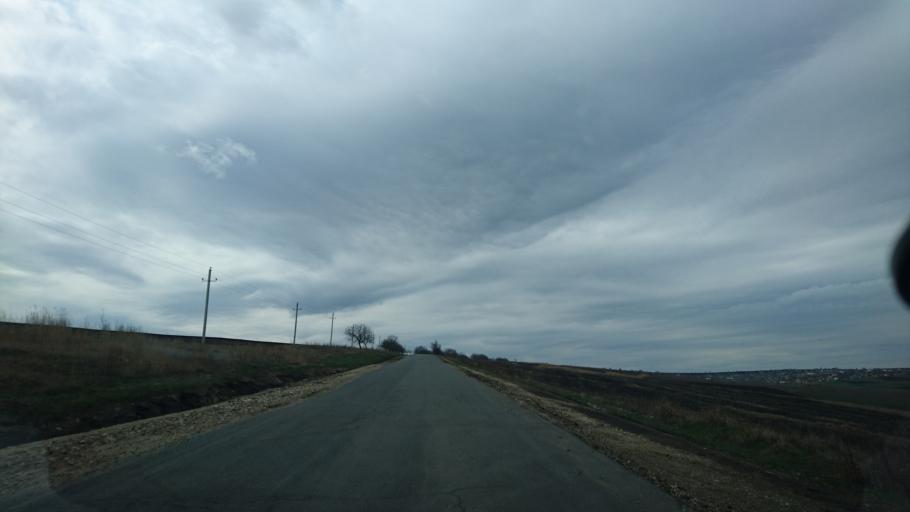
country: MD
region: Cantemir
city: Visniovca
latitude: 46.3367
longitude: 28.4353
